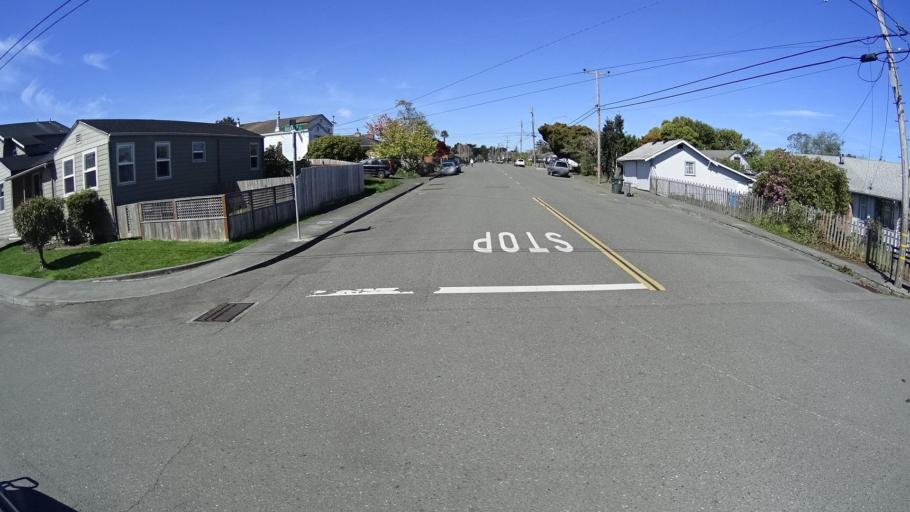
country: US
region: California
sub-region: Humboldt County
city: Myrtletown
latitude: 40.7923
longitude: -124.1263
